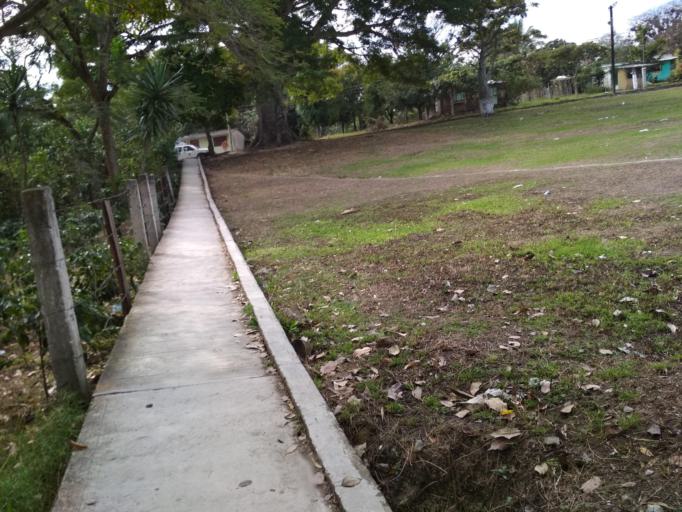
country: MX
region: Veracruz
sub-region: Coatepec
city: Tuzamapan
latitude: 19.3695
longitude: -96.8816
